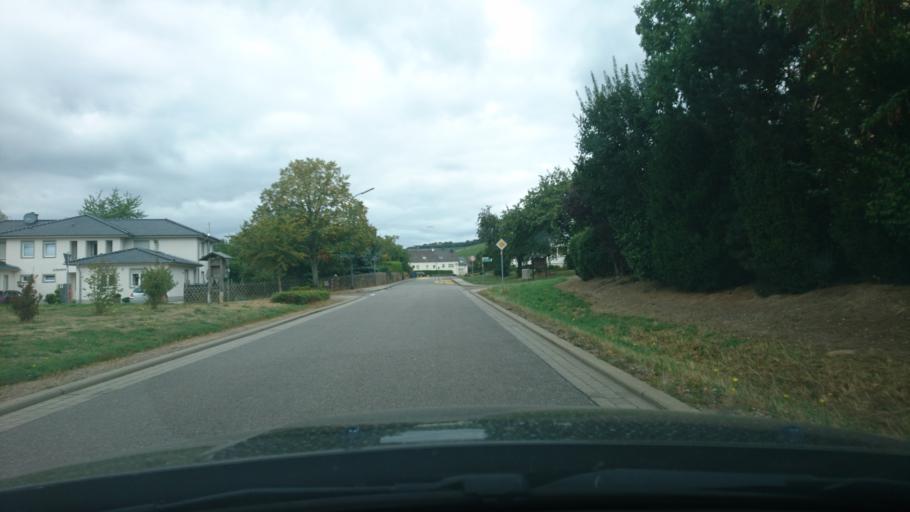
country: DE
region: Rheinland-Pfalz
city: Pellingen
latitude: 49.6786
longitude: 6.6382
